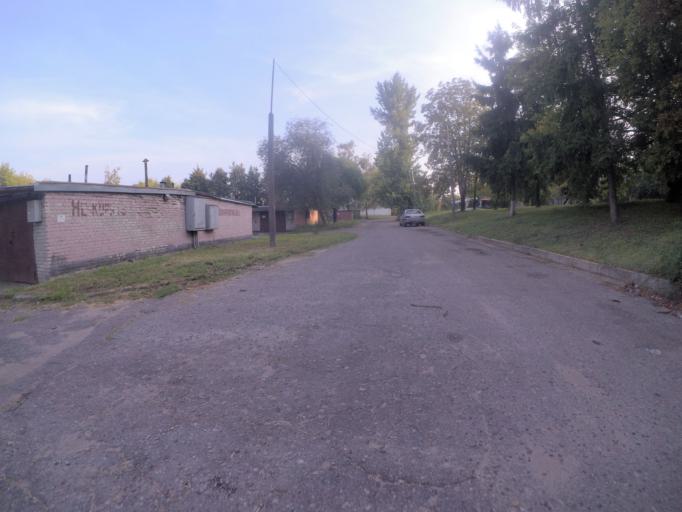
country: BY
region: Grodnenskaya
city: Hrodna
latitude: 53.6939
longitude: 23.8349
